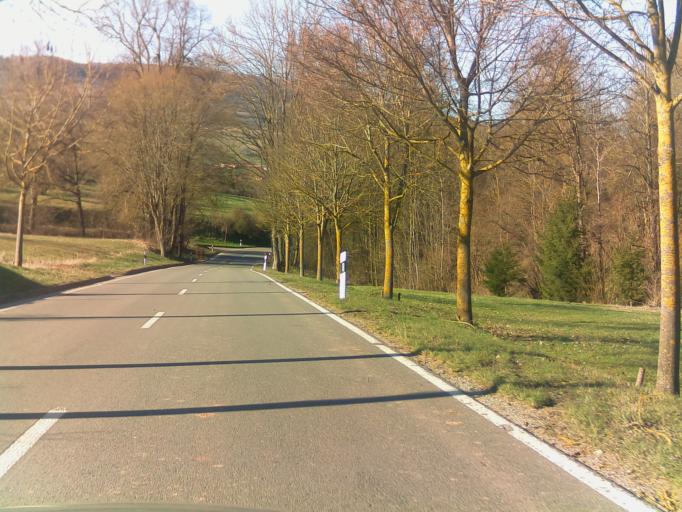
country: DE
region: Thuringia
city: Stepfershausen
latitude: 50.5482
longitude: 10.2854
